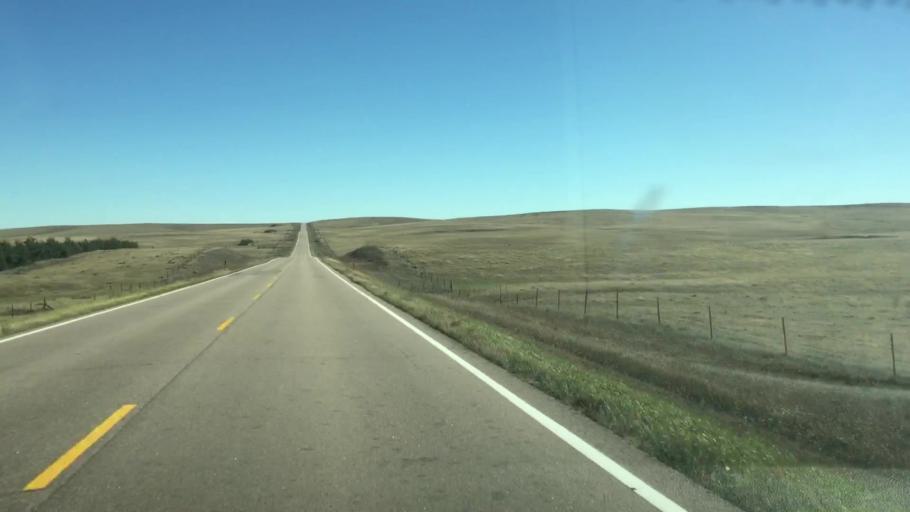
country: US
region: Colorado
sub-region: Lincoln County
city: Limon
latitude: 39.2784
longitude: -103.9971
